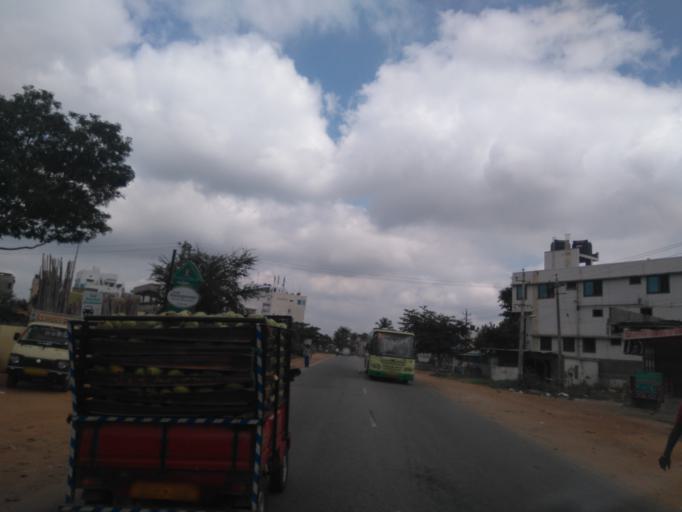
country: IN
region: Karnataka
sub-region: Mysore
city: Mysore
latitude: 12.2983
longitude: 76.6994
